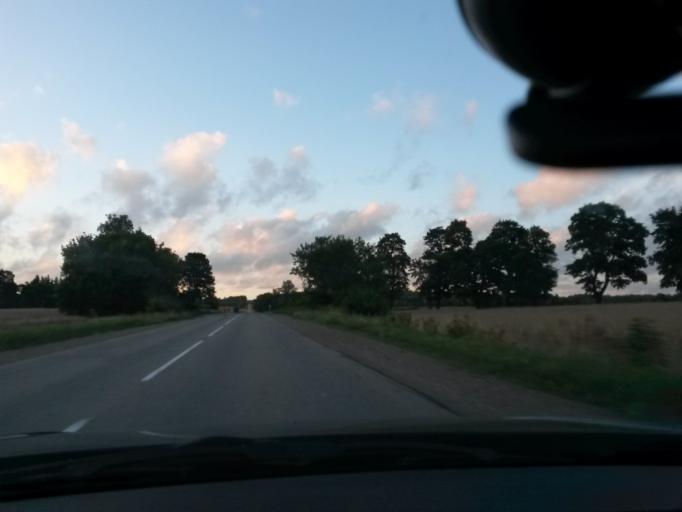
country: LV
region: Madonas Rajons
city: Madona
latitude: 56.7462
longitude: 26.0225
